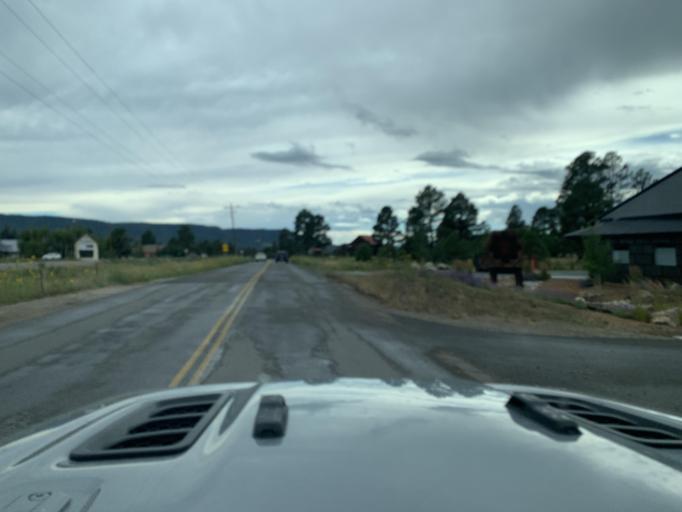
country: US
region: Colorado
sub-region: Archuleta County
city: Pagosa Springs
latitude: 37.2502
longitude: -107.0856
